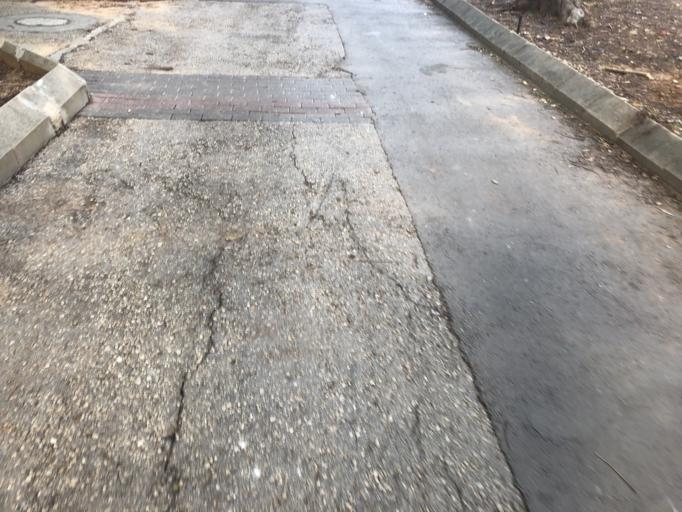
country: IL
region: Central District
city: Kfar Saba
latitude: 32.1765
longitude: 34.9101
